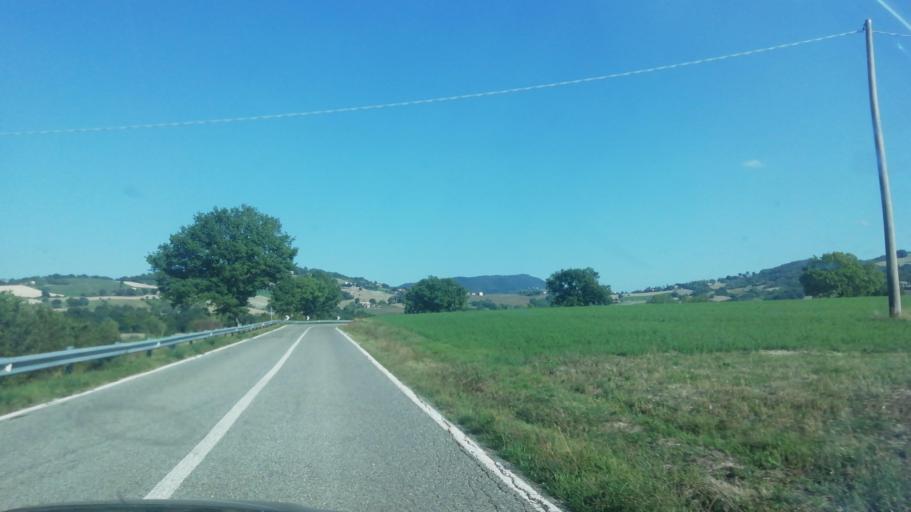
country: IT
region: The Marches
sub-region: Provincia di Pesaro e Urbino
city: Frontone
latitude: 43.5414
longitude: 12.7075
